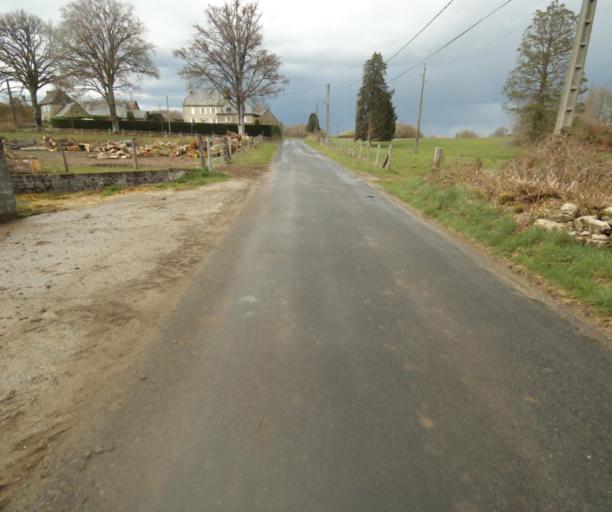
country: FR
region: Limousin
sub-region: Departement de la Correze
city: Egletons
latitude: 45.2582
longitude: 1.9912
